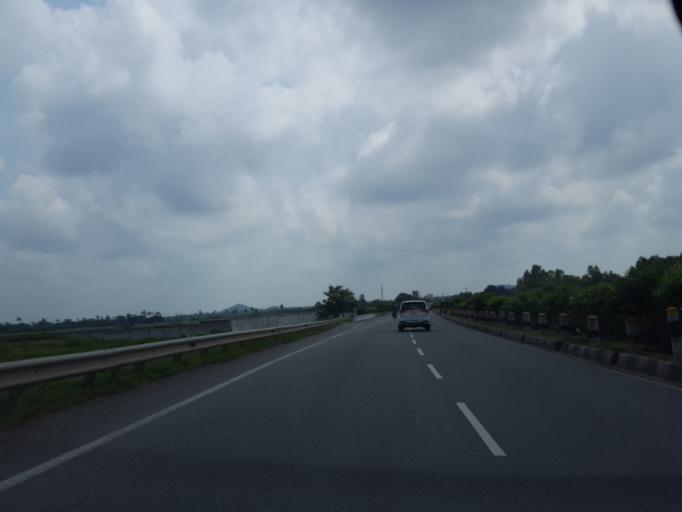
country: IN
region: Telangana
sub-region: Nalgonda
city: Bhongir
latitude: 17.2305
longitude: 79.0092
